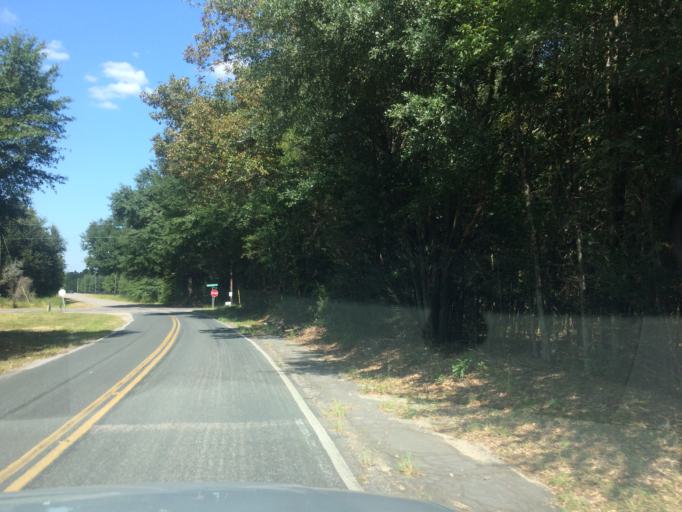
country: US
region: South Carolina
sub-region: Barnwell County
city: Williston
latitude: 33.6475
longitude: -81.4389
